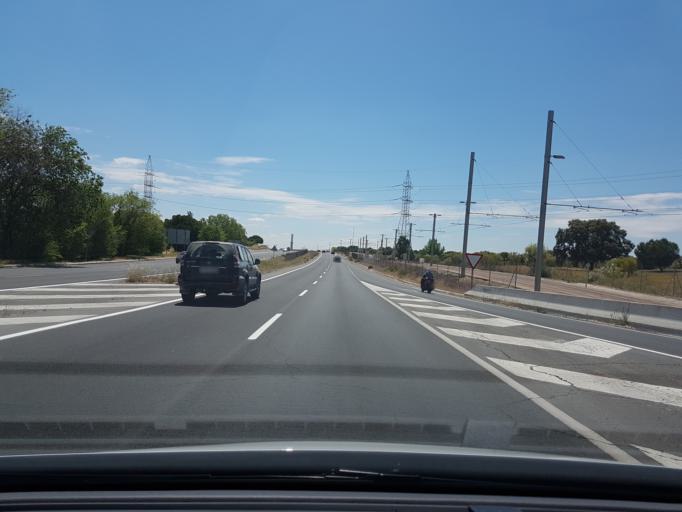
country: ES
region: Madrid
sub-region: Provincia de Madrid
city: Pozuelo de Alarcon
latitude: 40.4281
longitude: -3.8100
